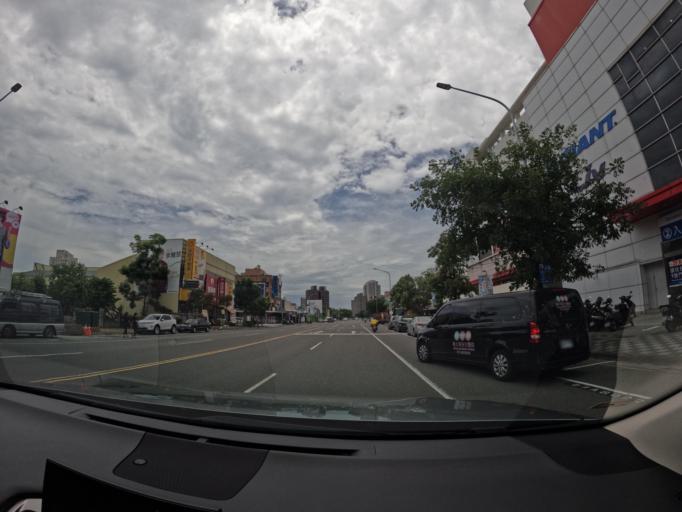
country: TW
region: Kaohsiung
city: Kaohsiung
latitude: 22.7274
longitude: 120.2912
